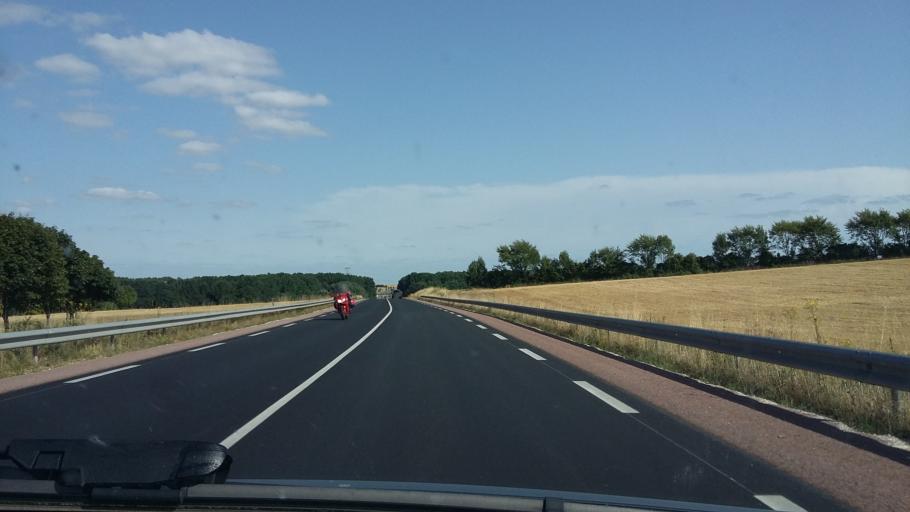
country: FR
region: Poitou-Charentes
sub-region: Departement de la Charente-Maritime
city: Saint-Jean-d'Angely
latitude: 45.9457
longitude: -0.4962
